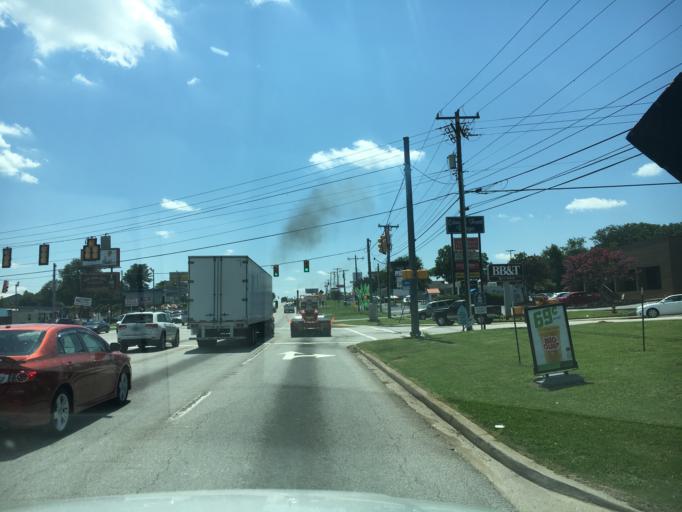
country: US
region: South Carolina
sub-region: Greenville County
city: Taylors
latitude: 34.9173
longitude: -82.3164
